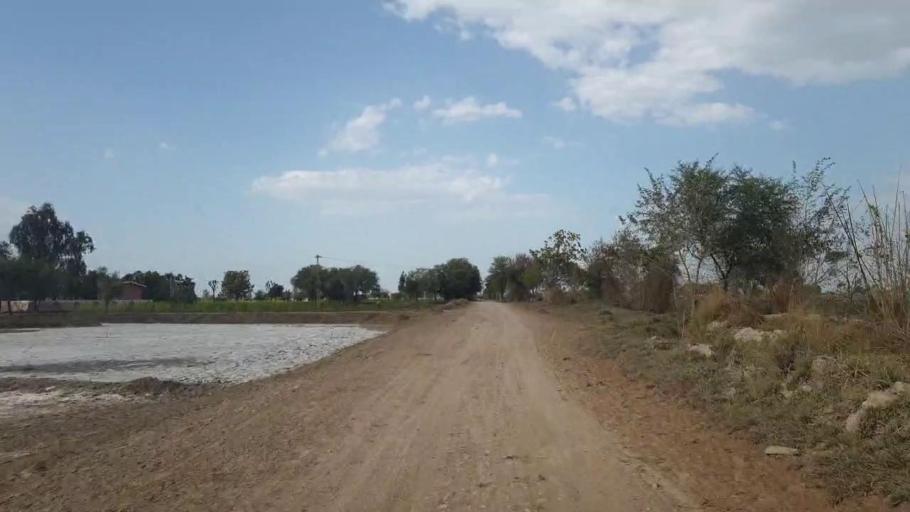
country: PK
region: Sindh
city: Shahdadpur
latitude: 26.0035
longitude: 68.4593
